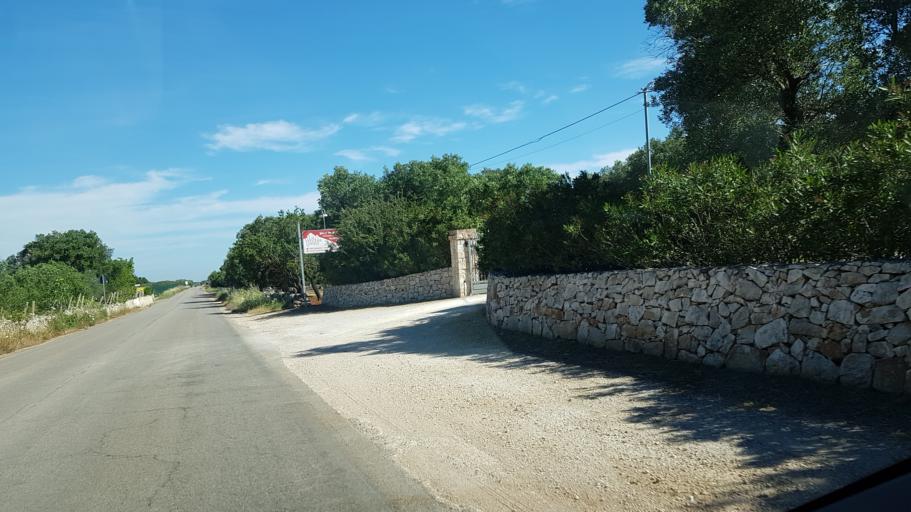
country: IT
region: Apulia
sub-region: Provincia di Brindisi
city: San Vito dei Normanni
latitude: 40.6334
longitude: 17.7316
